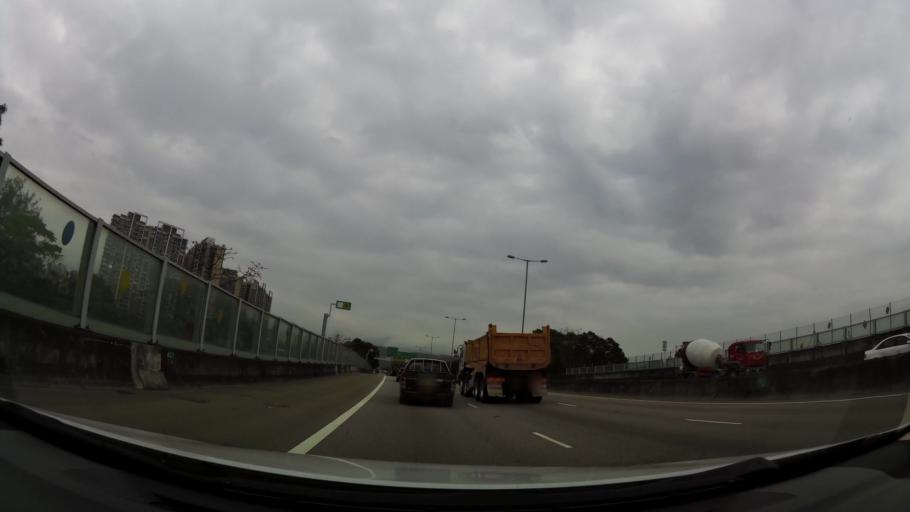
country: HK
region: Yuen Long
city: Yuen Long Kau Hui
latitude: 22.4359
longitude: 114.0198
